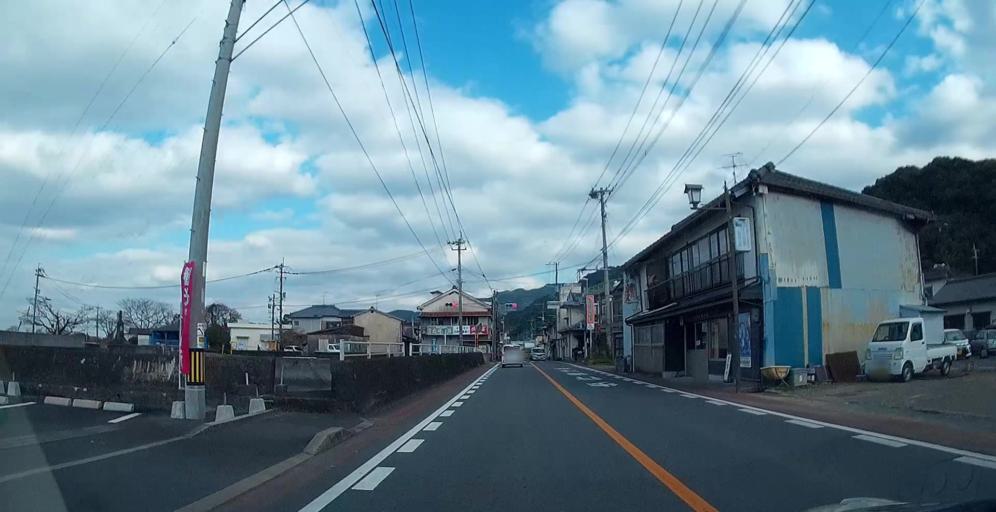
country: JP
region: Kumamoto
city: Yatsushiro
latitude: 32.4341
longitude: 130.5751
